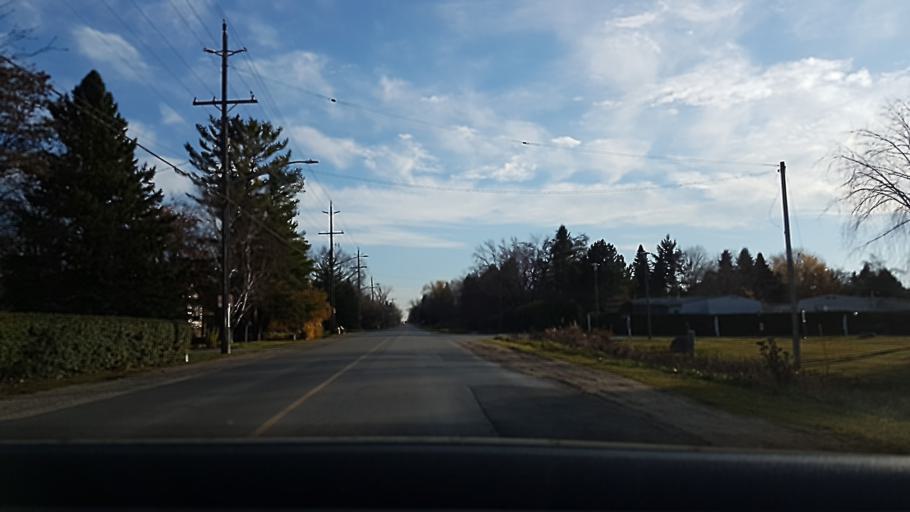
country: CA
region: Ontario
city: Innisfil
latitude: 44.3580
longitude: -79.5503
